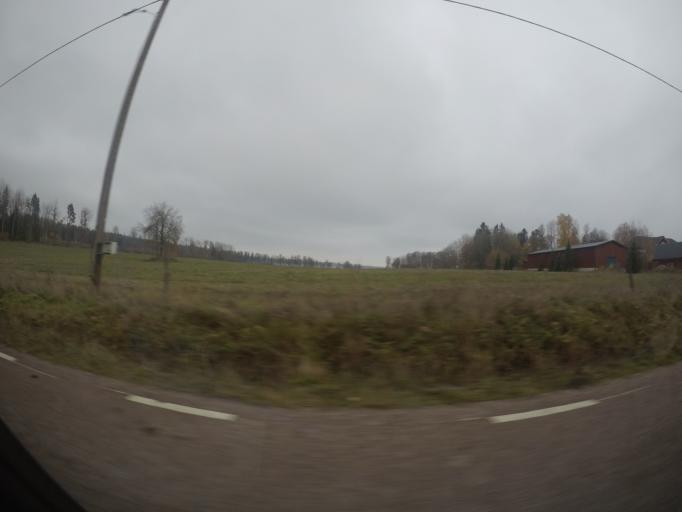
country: SE
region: Vaestmanland
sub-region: Surahammars Kommun
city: Ramnas
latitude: 59.6998
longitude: 16.0713
